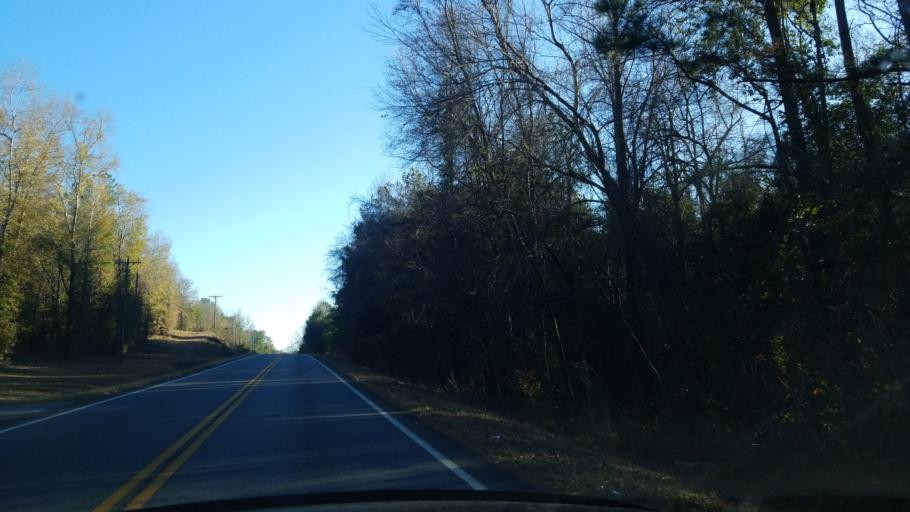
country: US
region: Georgia
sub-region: Talbot County
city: Talbotton
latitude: 32.5485
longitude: -84.6026
